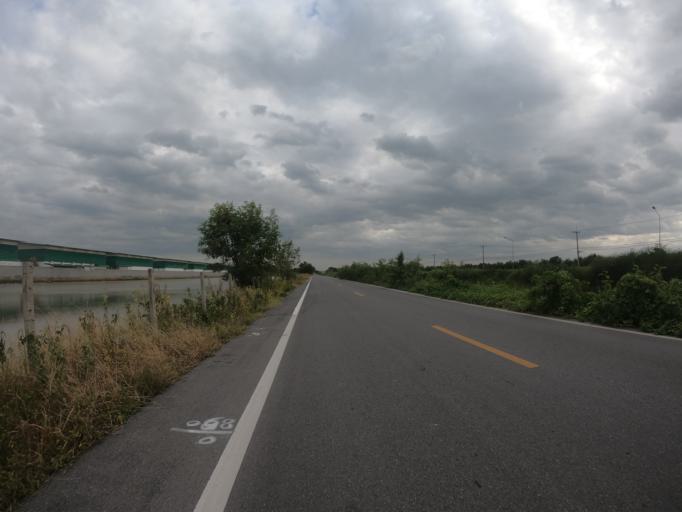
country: TH
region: Pathum Thani
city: Nong Suea
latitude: 14.0679
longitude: 100.8468
